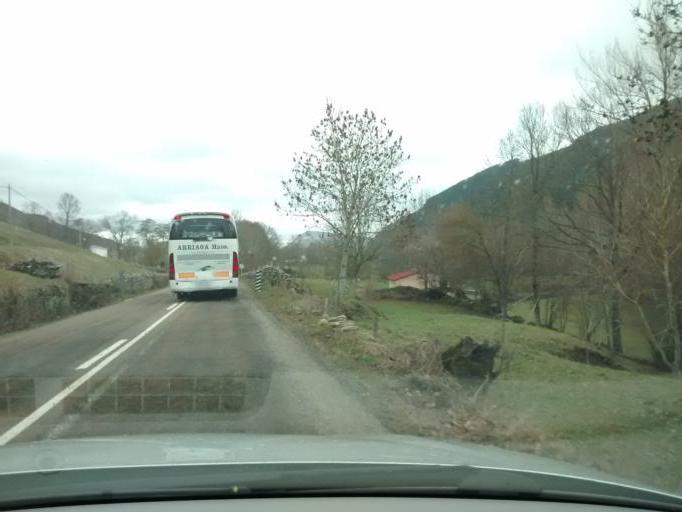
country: ES
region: Castille and Leon
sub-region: Provincia de Burgos
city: Espinosa de los Monteros
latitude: 43.1005
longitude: -3.5694
